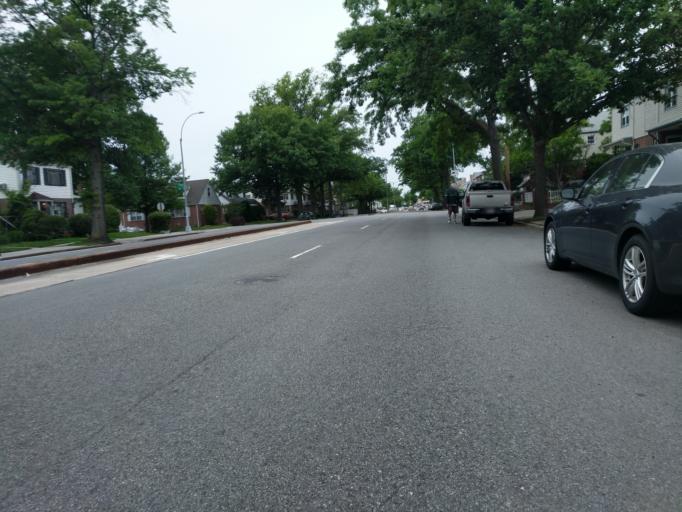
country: US
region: New York
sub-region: Nassau County
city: East Atlantic Beach
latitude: 40.7499
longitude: -73.7788
